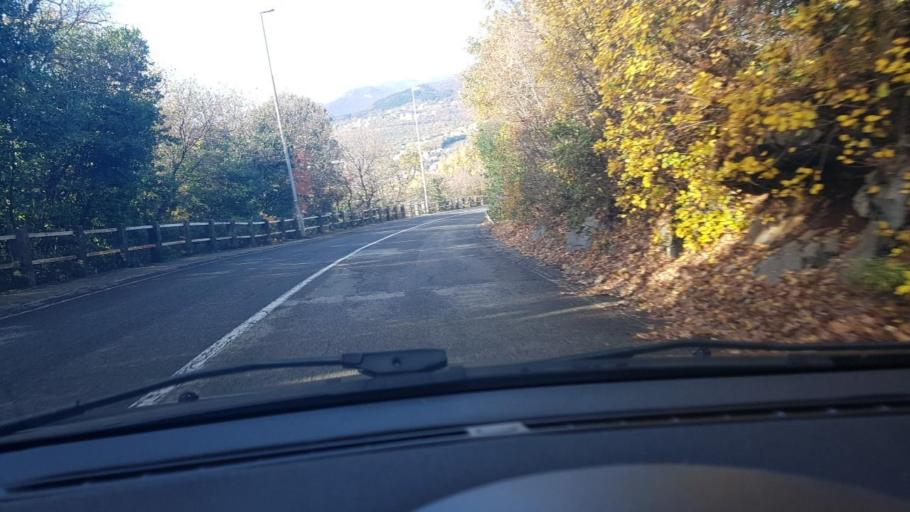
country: HR
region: Primorsko-Goranska
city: Rubesi
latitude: 45.3507
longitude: 14.3398
